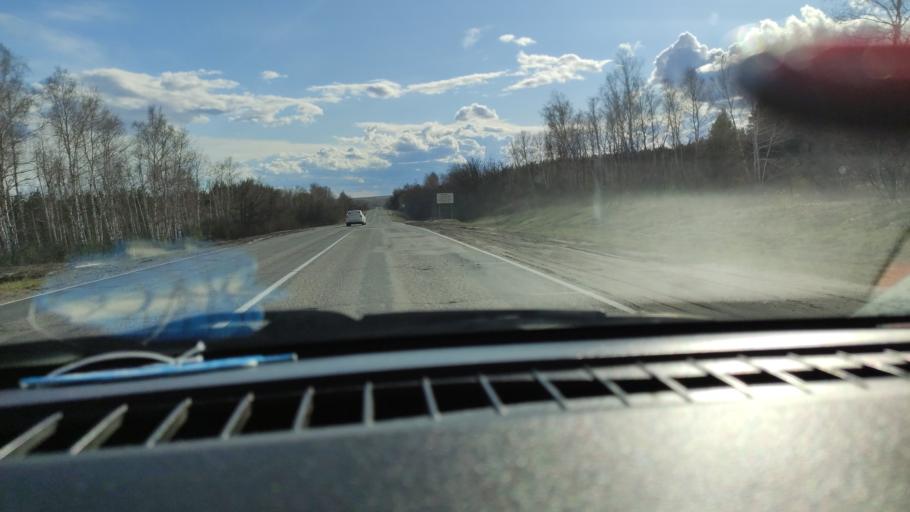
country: RU
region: Saratov
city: Sennoy
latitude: 52.1148
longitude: 46.8360
